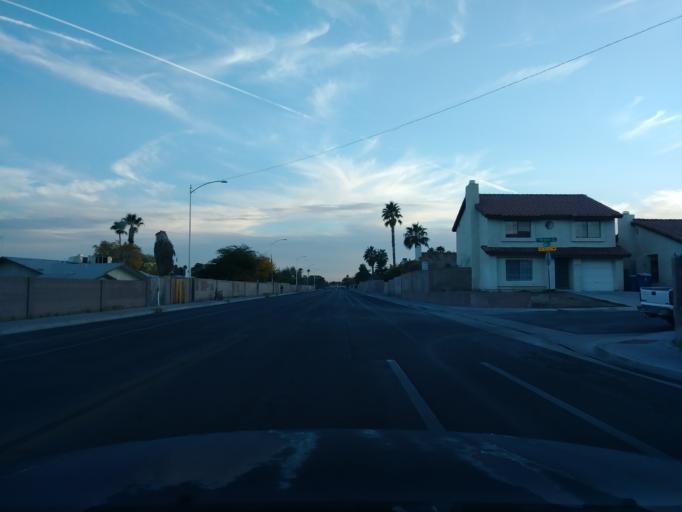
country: US
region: Nevada
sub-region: Clark County
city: Spring Valley
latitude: 36.1648
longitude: -115.2421
